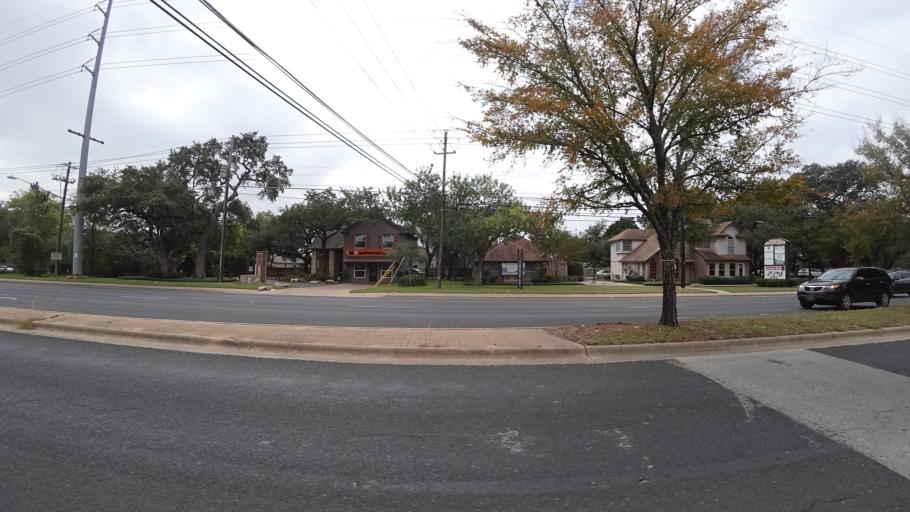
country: US
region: Texas
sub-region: Travis County
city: Shady Hollow
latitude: 30.1800
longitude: -97.8424
